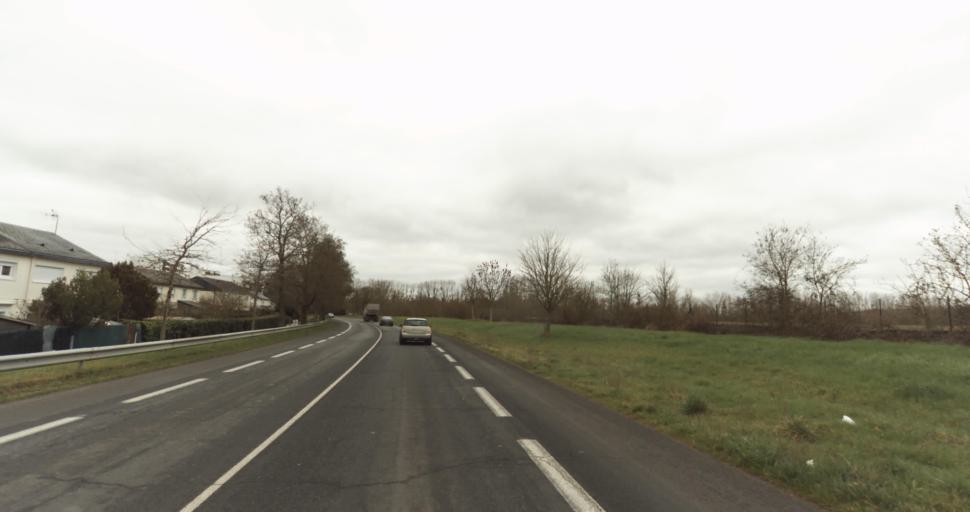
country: FR
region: Pays de la Loire
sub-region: Departement de Maine-et-Loire
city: Varrains
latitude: 47.2406
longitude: -0.0796
